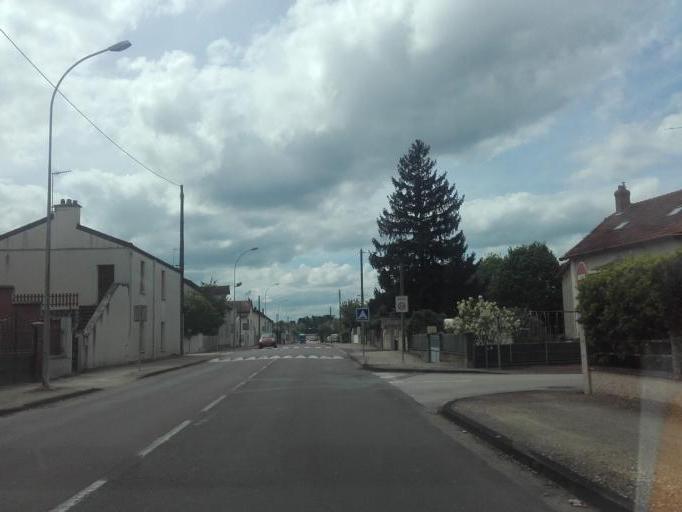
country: FR
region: Bourgogne
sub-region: Departement de Saone-et-Loire
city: Saint-Remy
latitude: 46.7741
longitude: 4.8264
